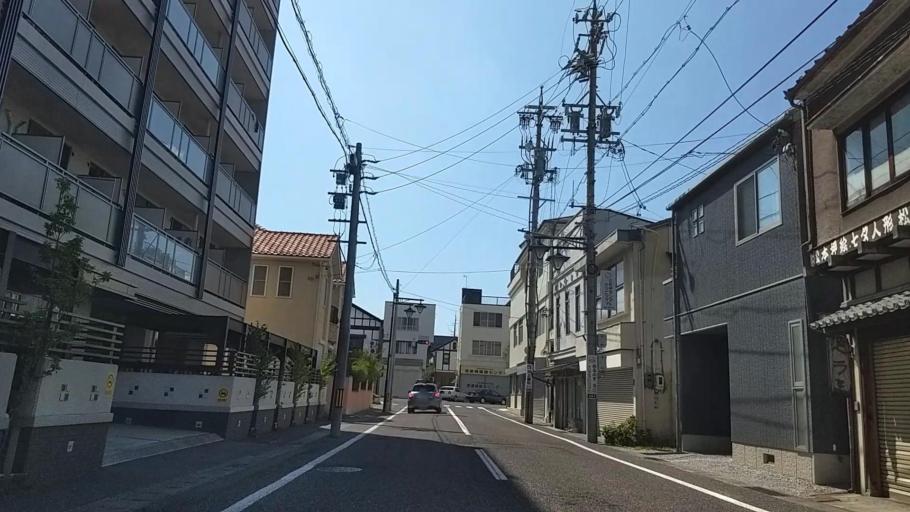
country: JP
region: Nagano
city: Matsumoto
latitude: 36.2317
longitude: 137.9735
